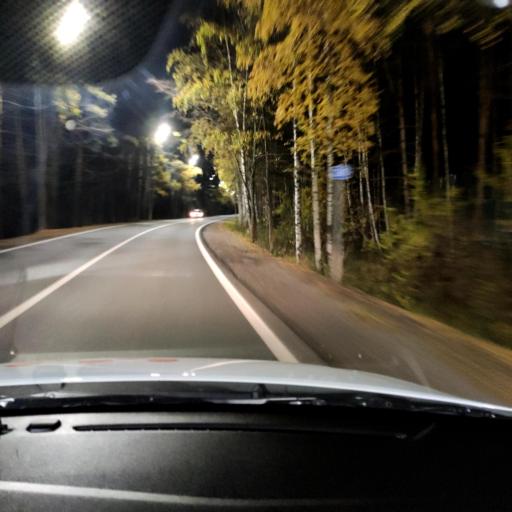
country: RU
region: Tatarstan
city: Verkhniy Uslon
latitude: 55.6334
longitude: 49.0185
